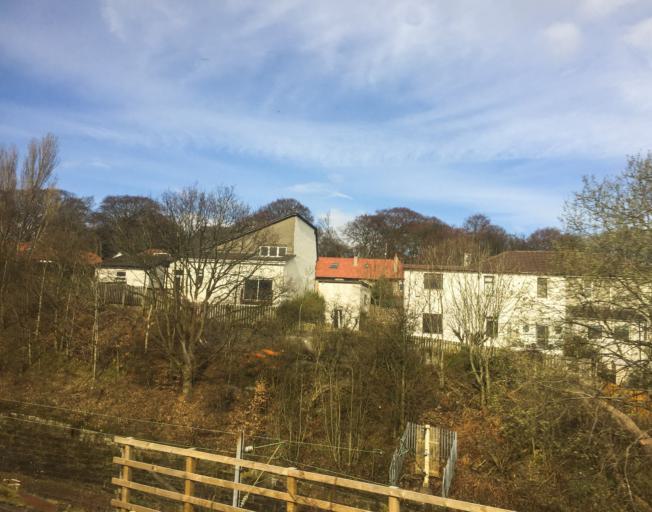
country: GB
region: Scotland
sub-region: East Dunbartonshire
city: Bearsden
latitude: 55.8989
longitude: -4.3231
